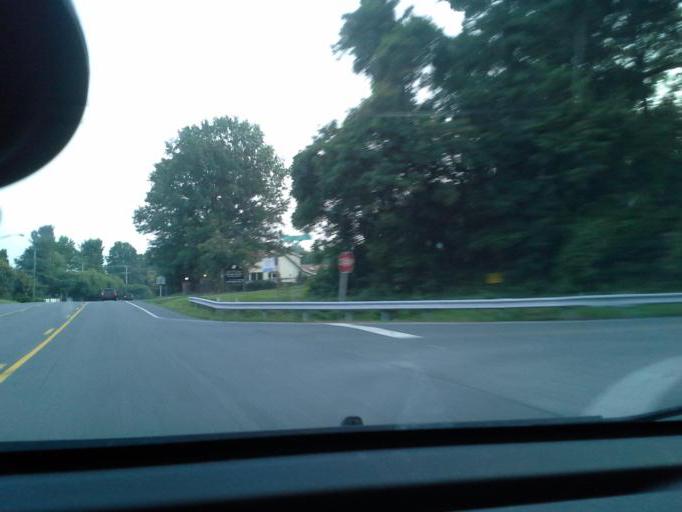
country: US
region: Maryland
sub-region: Anne Arundel County
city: Londontowne
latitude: 38.9111
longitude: -76.5801
